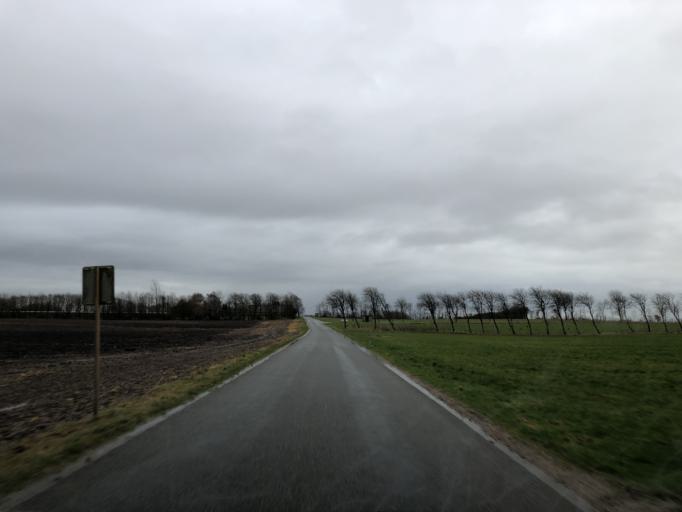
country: DK
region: Central Jutland
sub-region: Holstebro Kommune
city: Holstebro
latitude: 56.3794
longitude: 8.7273
